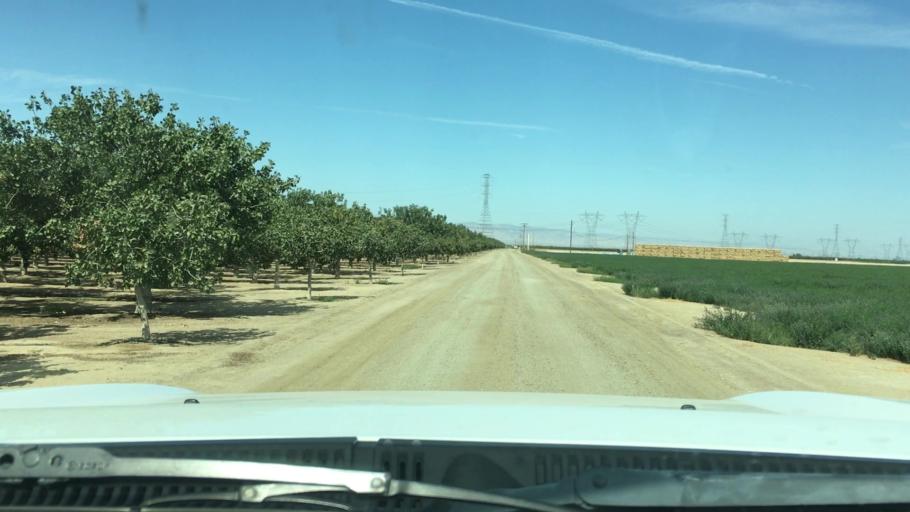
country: US
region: California
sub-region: Kern County
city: Buttonwillow
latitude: 35.3767
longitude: -119.3913
